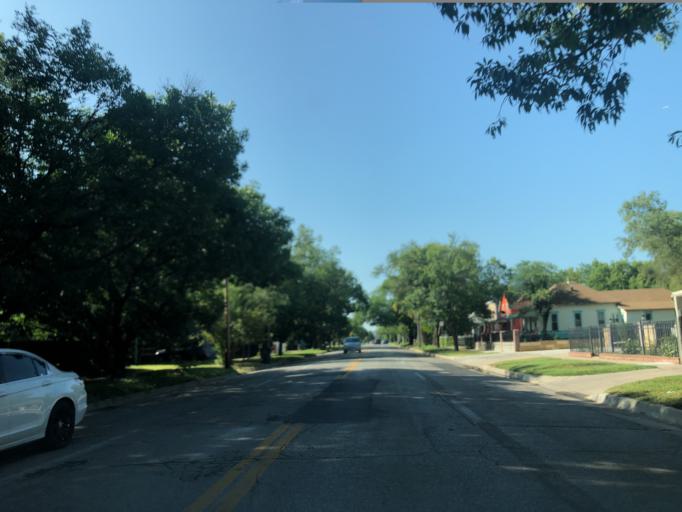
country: US
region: Kansas
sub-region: Sedgwick County
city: Wichita
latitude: 37.7044
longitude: -97.3420
